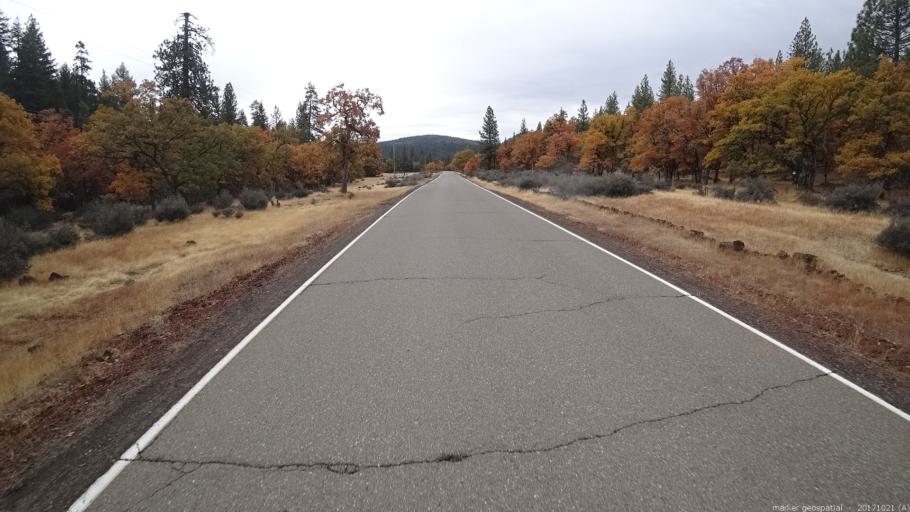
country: US
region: California
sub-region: Shasta County
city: Burney
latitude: 41.0366
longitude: -121.6718
